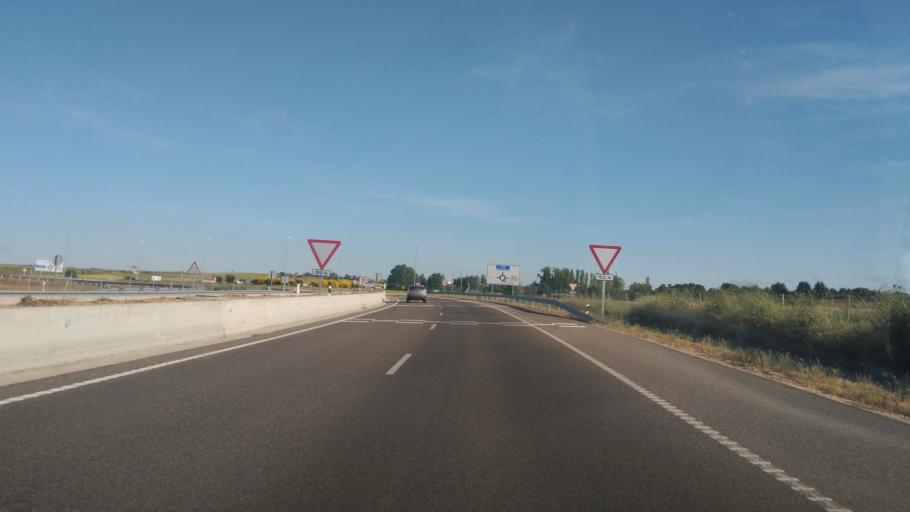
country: ES
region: Castille and Leon
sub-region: Provincia de Zamora
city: Morales del Vino
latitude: 41.4603
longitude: -5.7328
